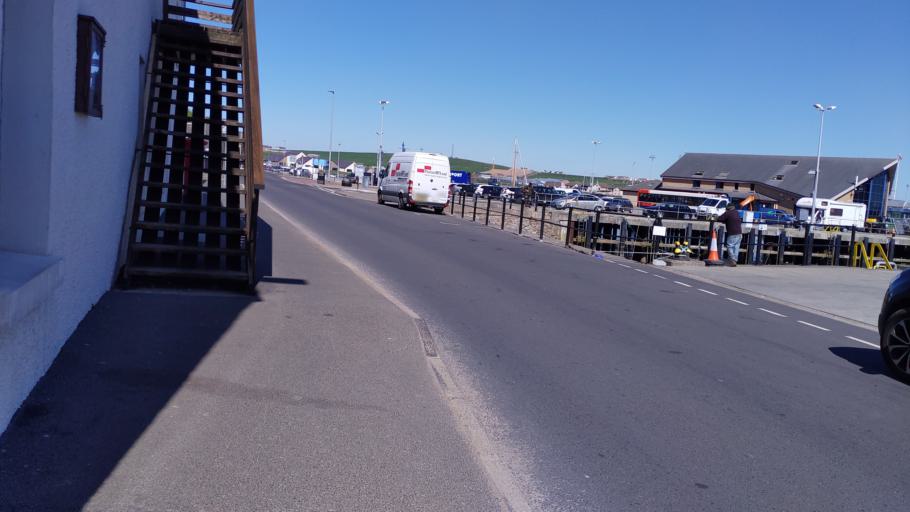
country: GB
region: Scotland
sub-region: Orkney Islands
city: Stromness
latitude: 58.9636
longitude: -3.2972
